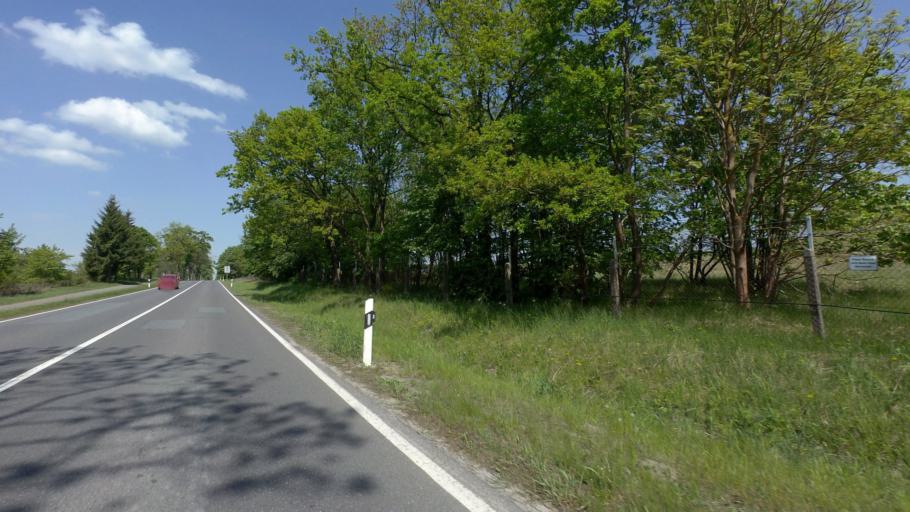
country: DE
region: Mecklenburg-Vorpommern
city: Neustrelitz
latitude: 53.3970
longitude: 13.0438
